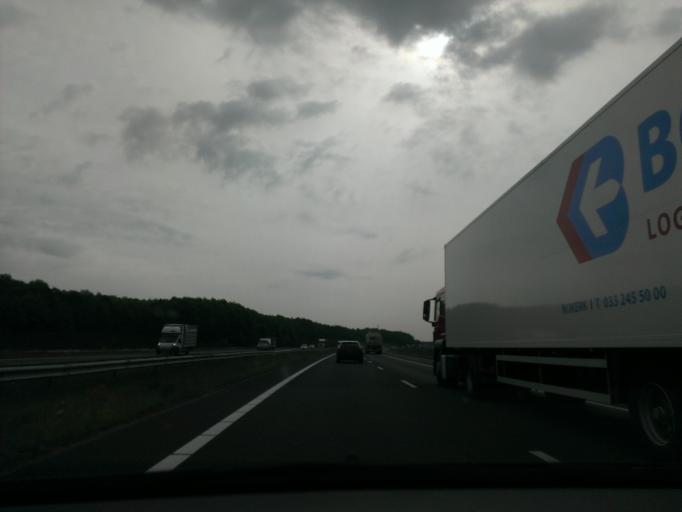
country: NL
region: Overijssel
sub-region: Gemeente Hof van Twente
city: Markelo
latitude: 52.2839
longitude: 6.5220
